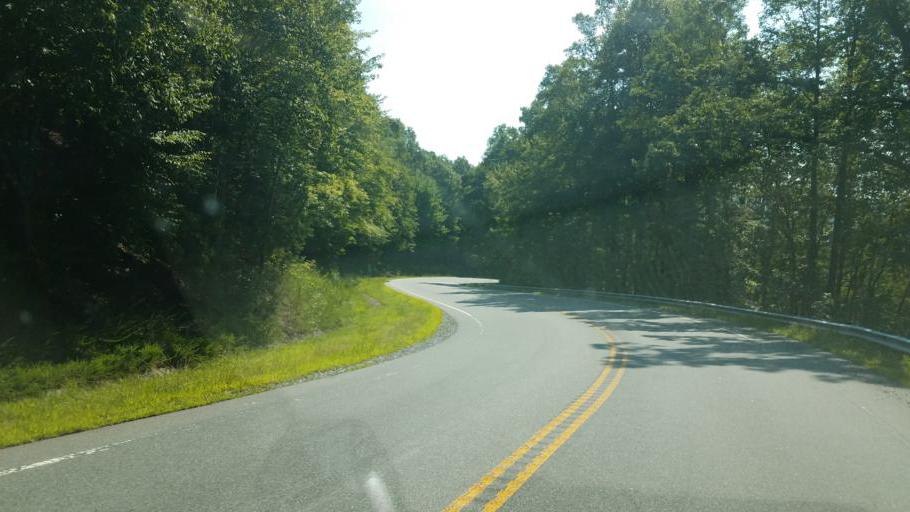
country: US
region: North Carolina
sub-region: Avery County
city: Newland
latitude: 35.9229
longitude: -81.8192
